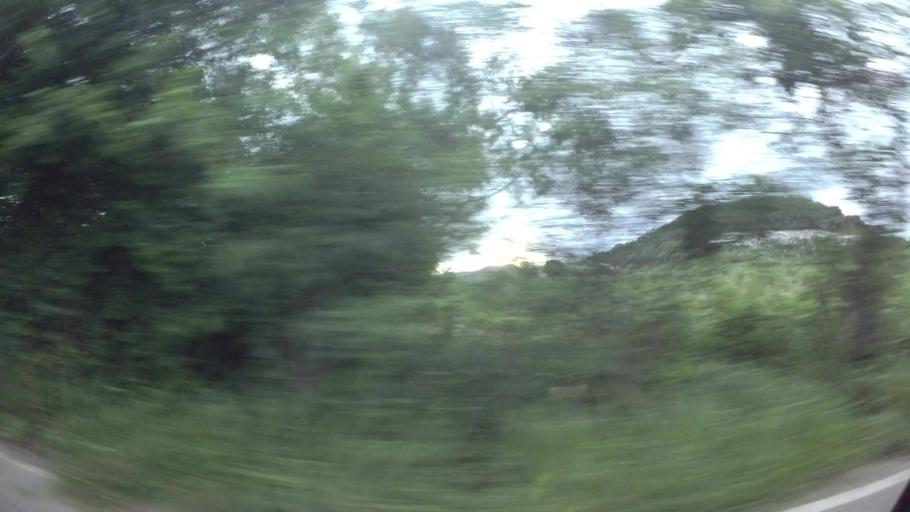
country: TH
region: Chon Buri
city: Sattahip
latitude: 12.6973
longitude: 100.9025
